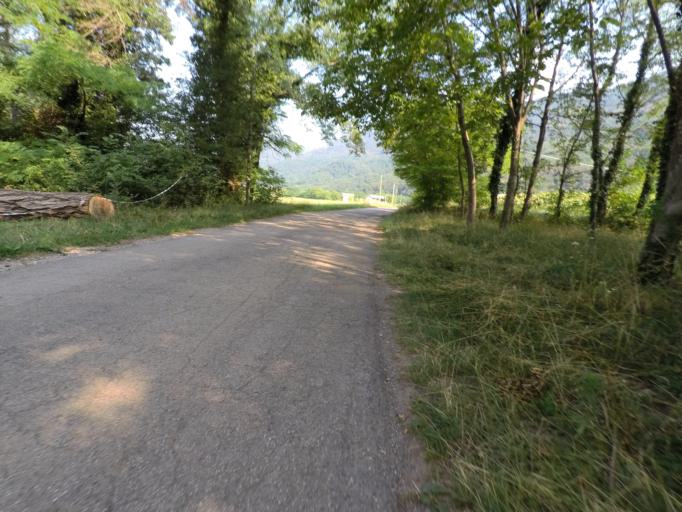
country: IT
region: Friuli Venezia Giulia
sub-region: Provincia di Pordenone
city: Meduno
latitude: 46.2088
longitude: 12.8119
